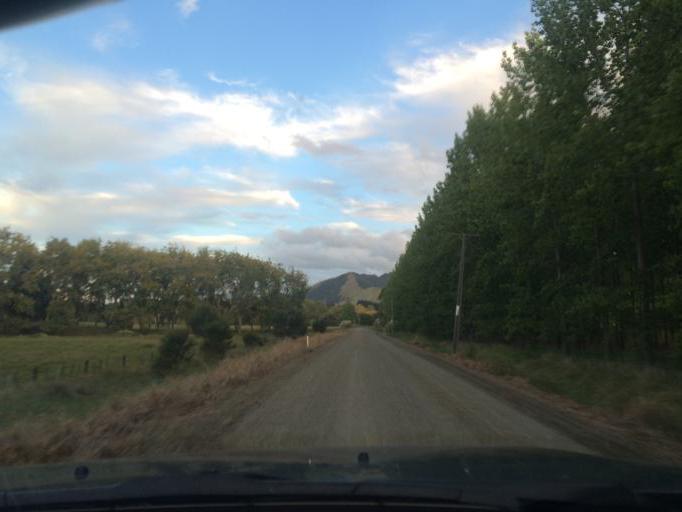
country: NZ
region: Northland
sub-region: Whangarei
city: Maungatapere
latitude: -35.8164
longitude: 174.0370
